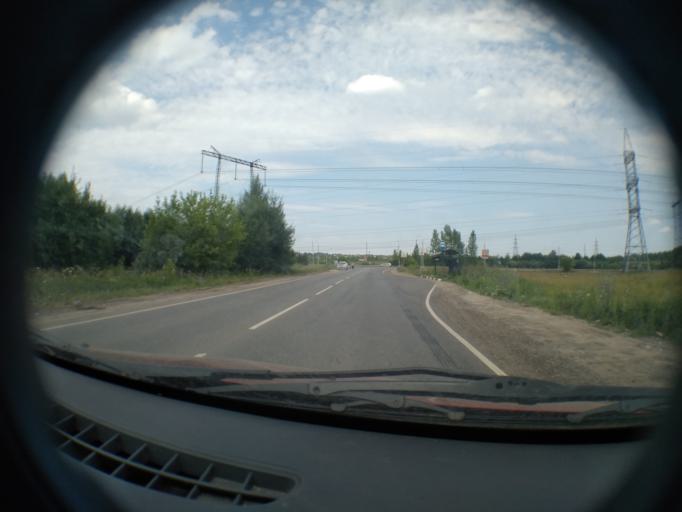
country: RU
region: Moskovskaya
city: Ostrovtsy
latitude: 55.5311
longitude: 37.9998
